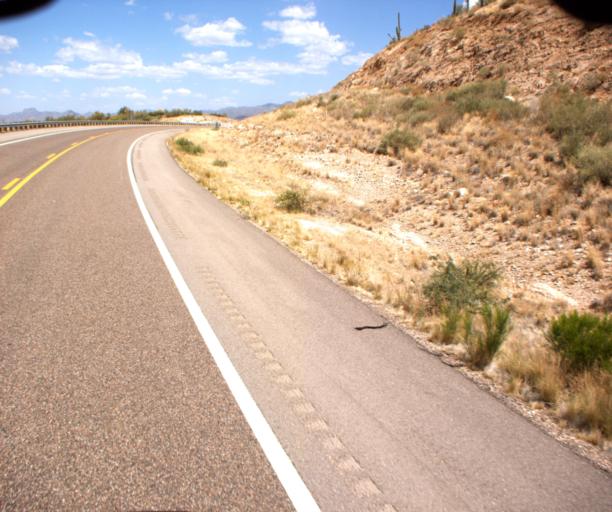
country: US
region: Arizona
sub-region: Pinal County
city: Superior
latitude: 33.2359
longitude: -111.0945
